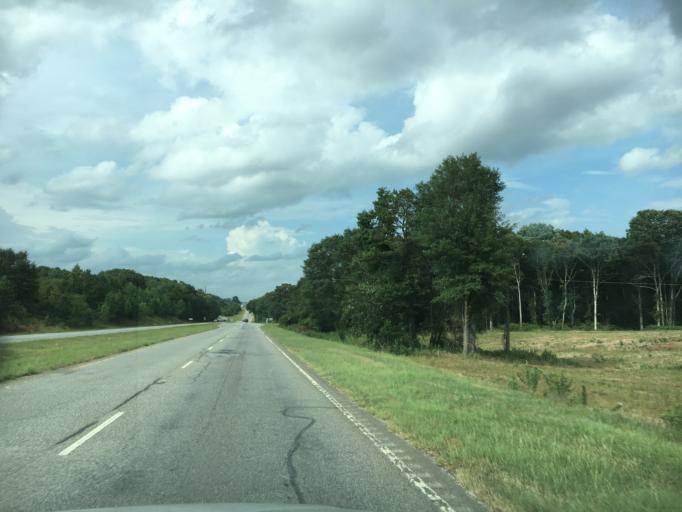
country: US
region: South Carolina
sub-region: Anderson County
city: Piedmont
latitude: 34.6831
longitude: -82.5066
